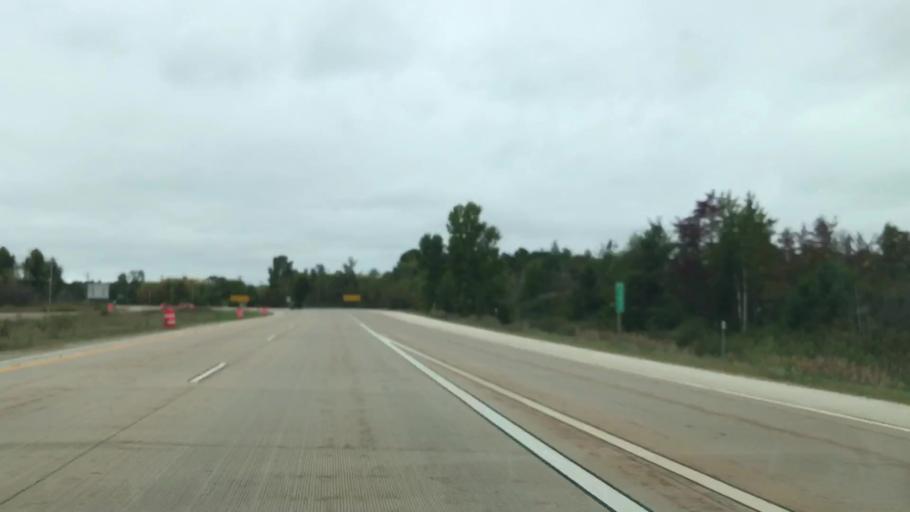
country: US
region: Wisconsin
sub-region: Oconto County
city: Oconto
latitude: 44.8686
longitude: -87.8980
